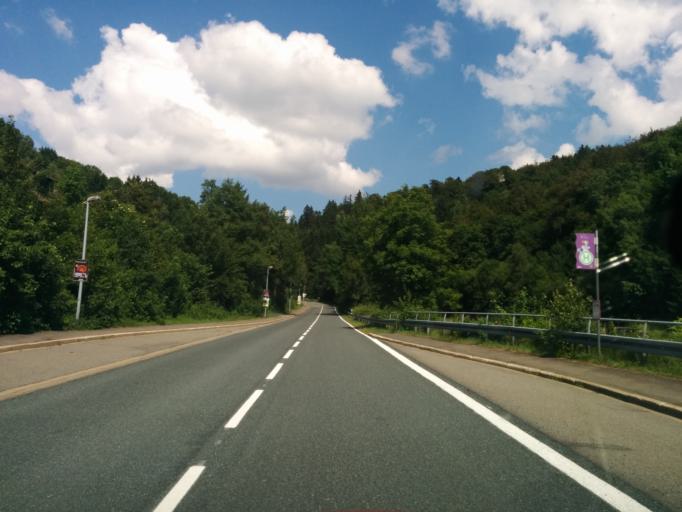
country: DE
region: Lower Saxony
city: Sankt Andreasberg
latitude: 51.7083
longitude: 10.5226
